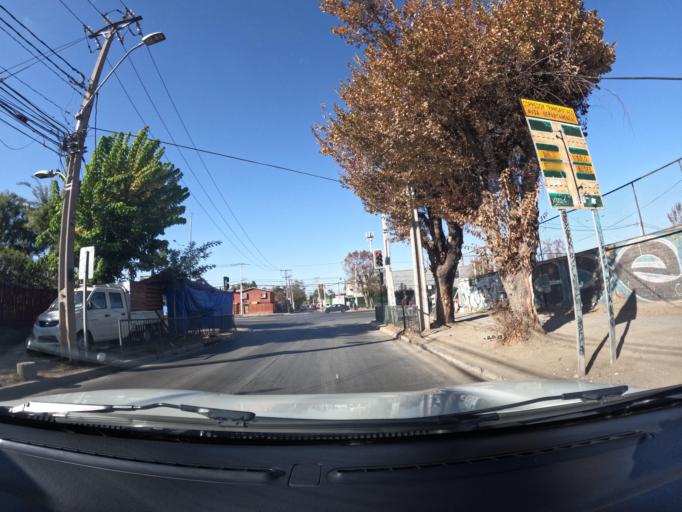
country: CL
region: Santiago Metropolitan
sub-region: Provincia de Santiago
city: Villa Presidente Frei, Nunoa, Santiago, Chile
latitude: -33.5105
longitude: -70.5761
